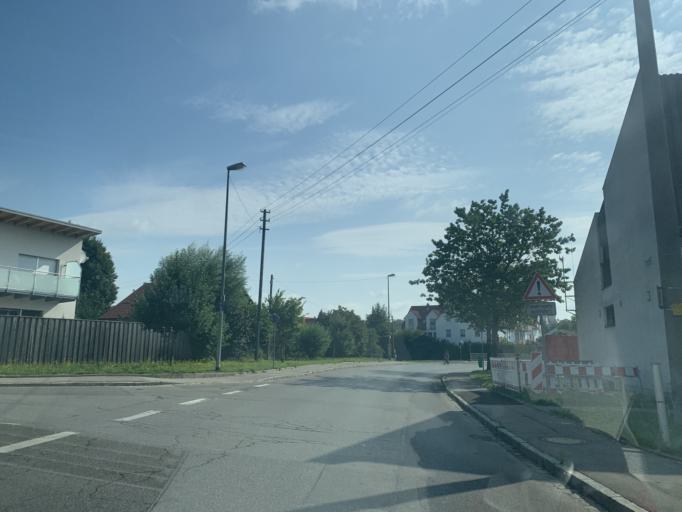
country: DE
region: Bavaria
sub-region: Swabia
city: Kissing
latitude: 48.2958
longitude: 10.9840
